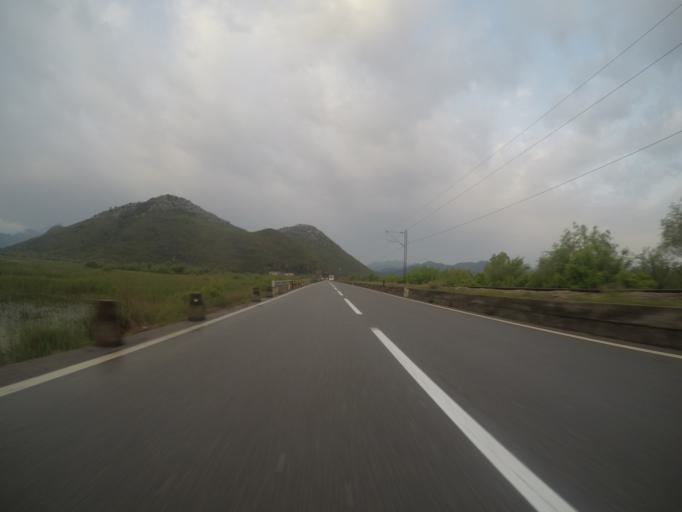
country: ME
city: Mojanovici
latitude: 42.2853
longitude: 19.1439
